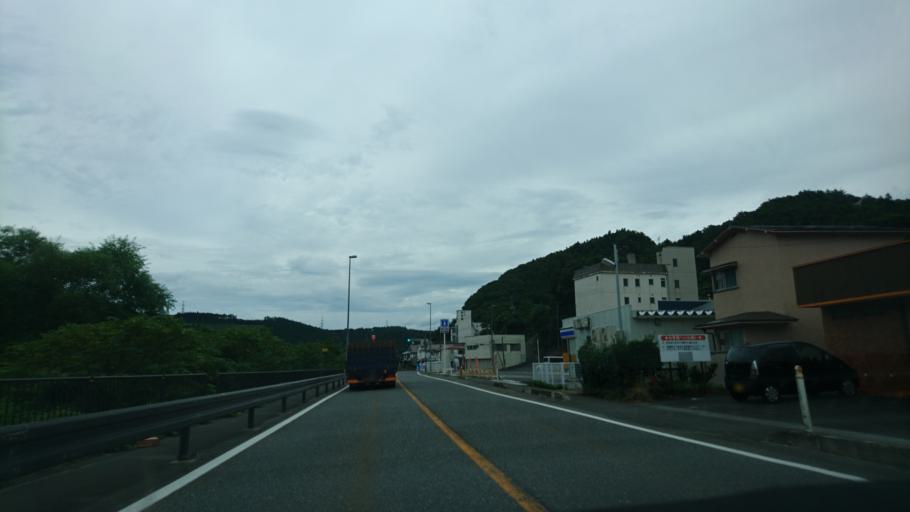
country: JP
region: Miyagi
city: Furukawa
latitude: 38.7489
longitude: 140.7266
